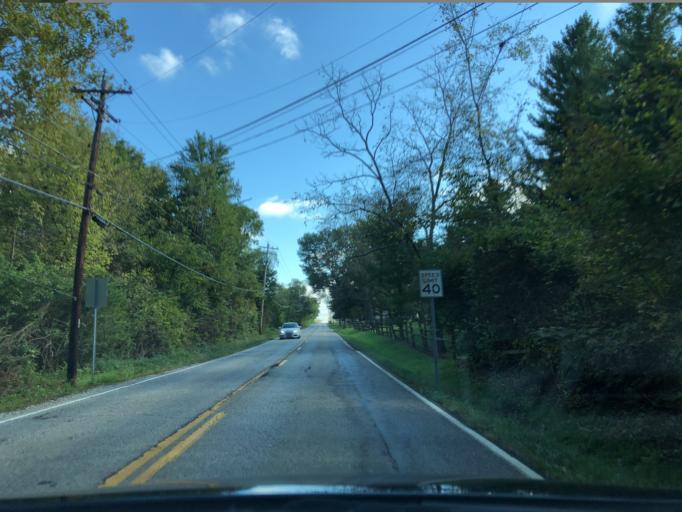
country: US
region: Ohio
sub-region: Hamilton County
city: Loveland
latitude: 39.2335
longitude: -84.2613
